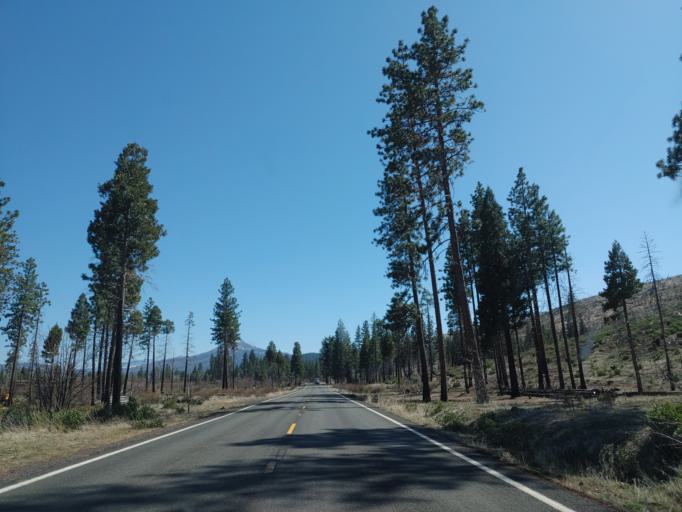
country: US
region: California
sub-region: Shasta County
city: Burney
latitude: 40.7857
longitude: -121.5053
